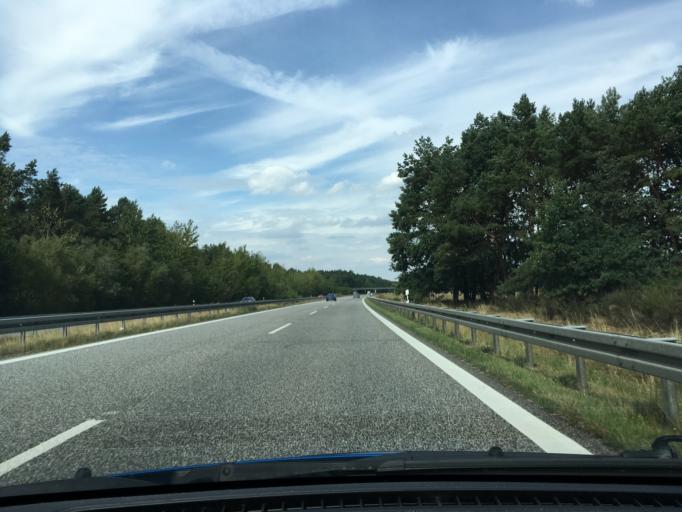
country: DE
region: Mecklenburg-Vorpommern
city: Mirow
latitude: 53.4902
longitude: 11.4814
